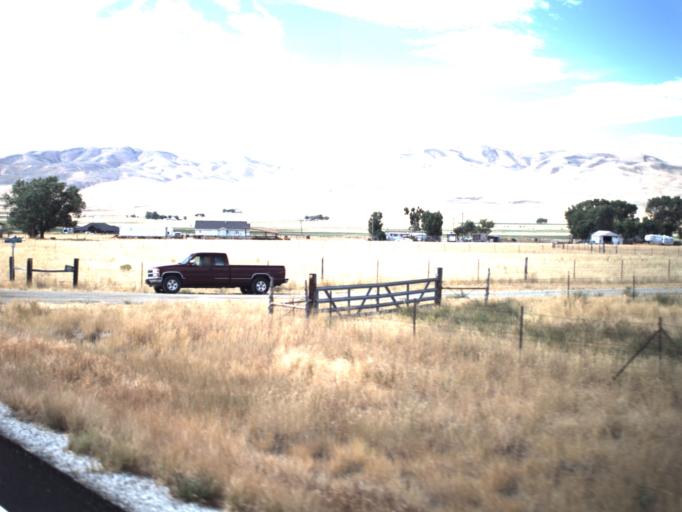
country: US
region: Utah
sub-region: Box Elder County
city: Garland
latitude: 41.7860
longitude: -112.4308
